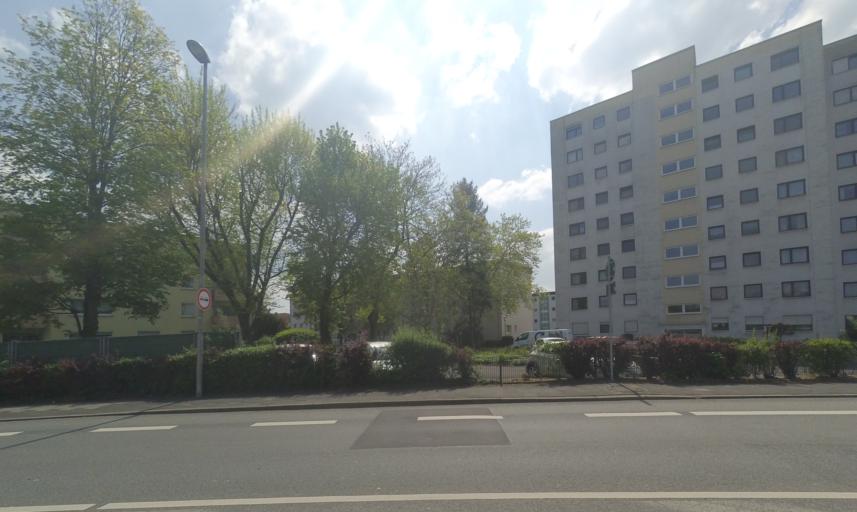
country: DE
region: Hesse
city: Heusenstamm
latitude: 50.0589
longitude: 8.7860
